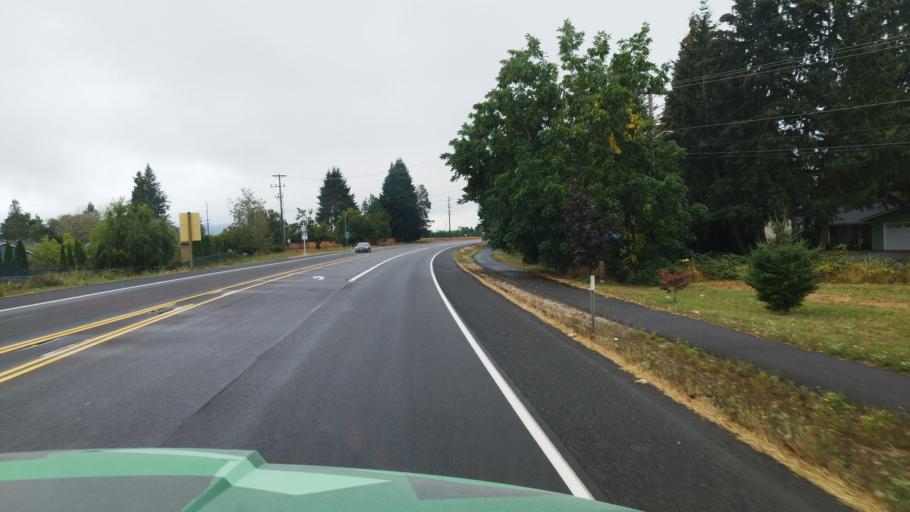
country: US
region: Oregon
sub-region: Washington County
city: Forest Grove
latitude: 45.5162
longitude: -123.0858
